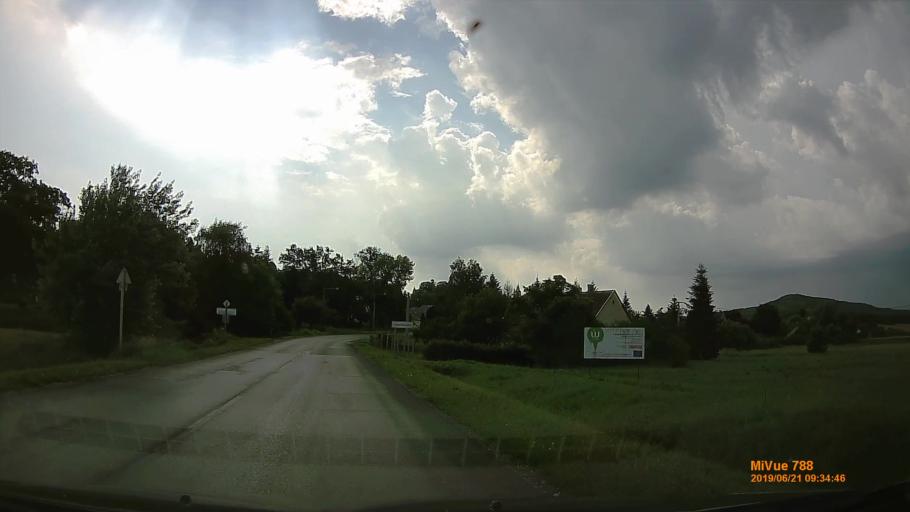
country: HU
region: Somogy
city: Taszar
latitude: 46.3245
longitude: 17.8904
